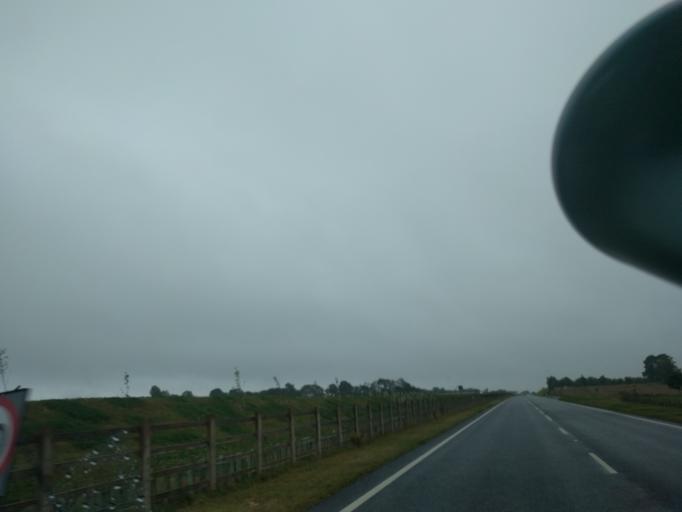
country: GB
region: England
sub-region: North Yorkshire
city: Bedale
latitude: 54.3284
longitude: -1.5852
